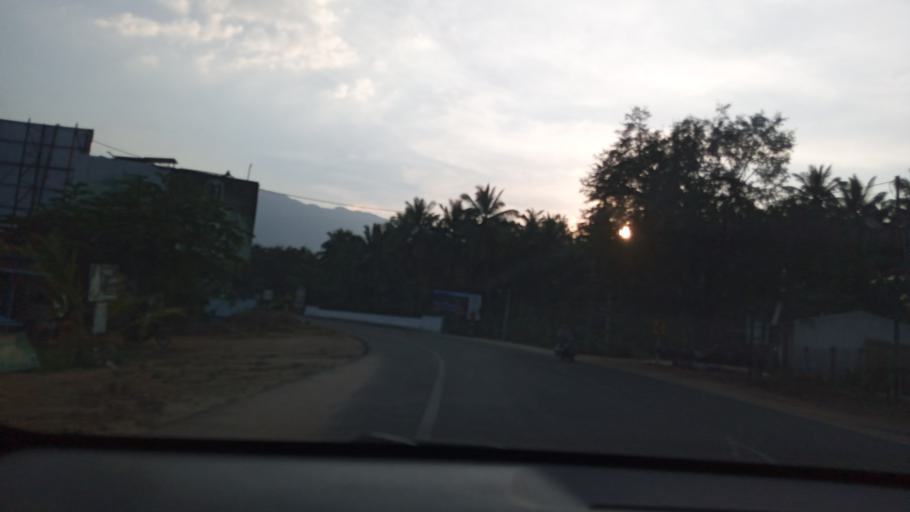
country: IN
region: Tamil Nadu
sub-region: Coimbatore
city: Perur
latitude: 10.9457
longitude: 76.7717
